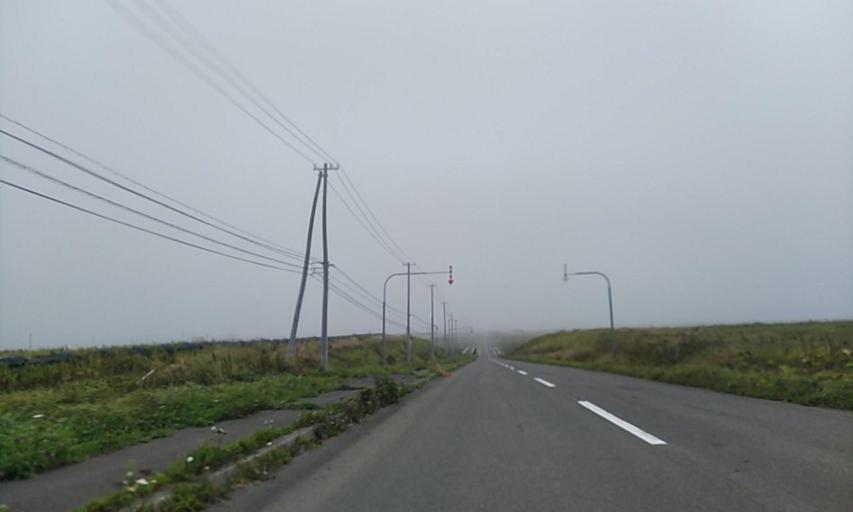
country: JP
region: Hokkaido
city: Nemuro
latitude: 43.3807
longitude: 145.7188
